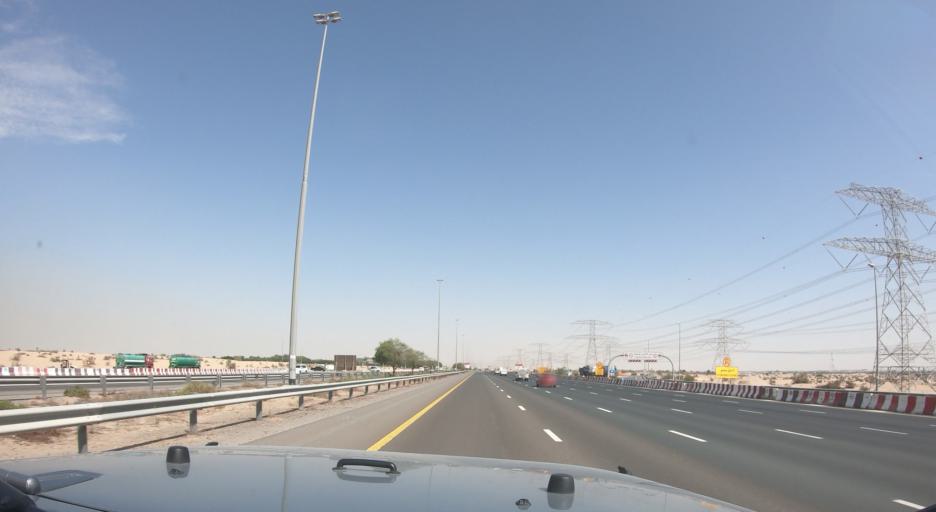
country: AE
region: Ash Shariqah
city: Sharjah
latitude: 25.1836
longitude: 55.5224
